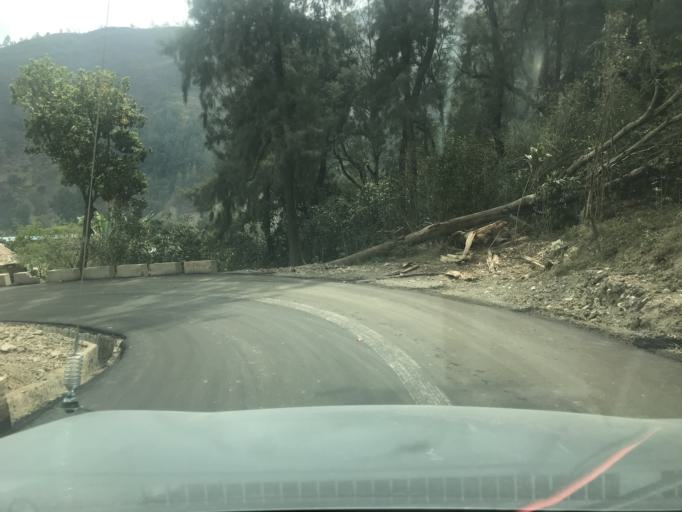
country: TL
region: Manufahi
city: Same
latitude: -8.8956
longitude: 125.5917
